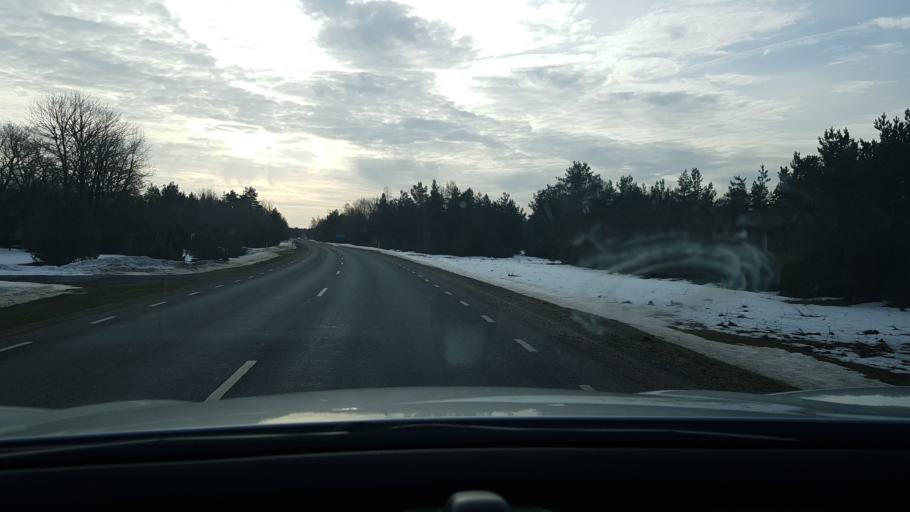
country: EE
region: Saare
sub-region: Kuressaare linn
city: Kuressaare
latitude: 58.2873
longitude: 22.5397
